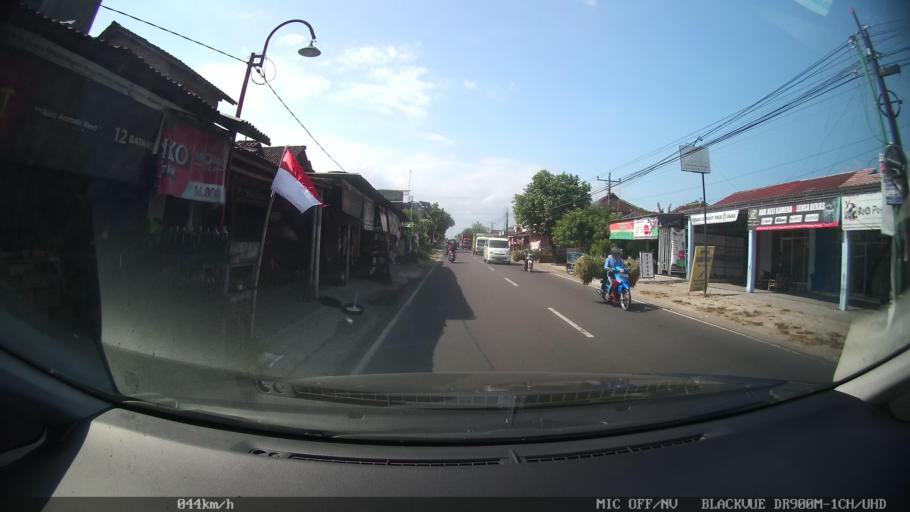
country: ID
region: Daerah Istimewa Yogyakarta
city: Sewon
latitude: -7.8901
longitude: 110.3865
